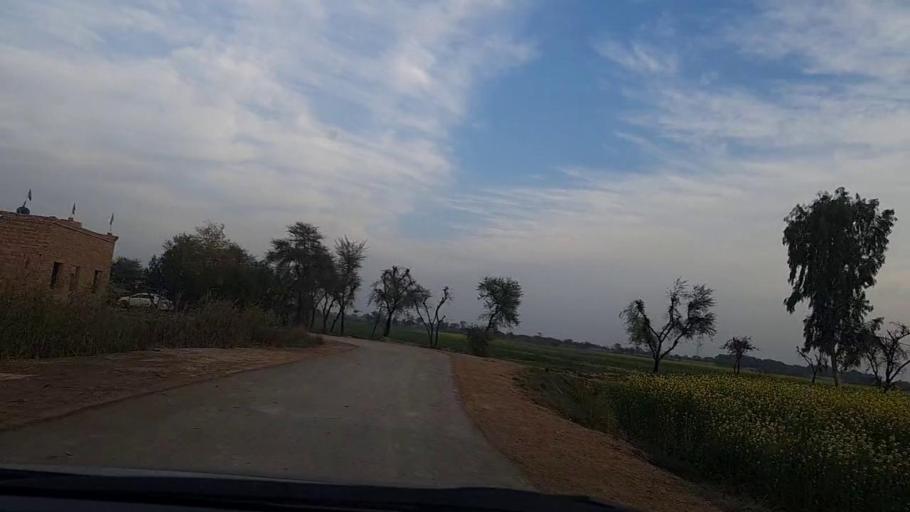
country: PK
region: Sindh
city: Sakrand
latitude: 26.1845
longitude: 68.3304
